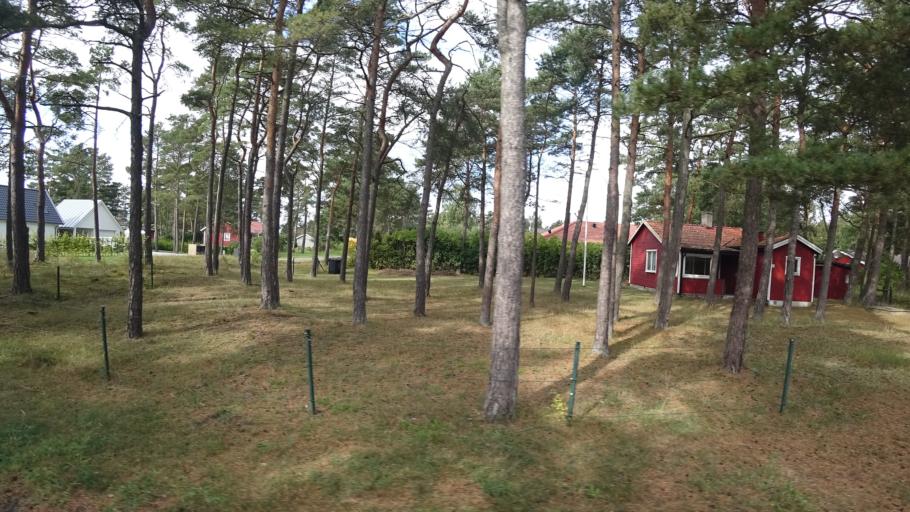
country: SE
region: Skane
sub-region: Kristianstads Kommun
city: Ahus
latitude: 55.9373
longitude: 14.2991
